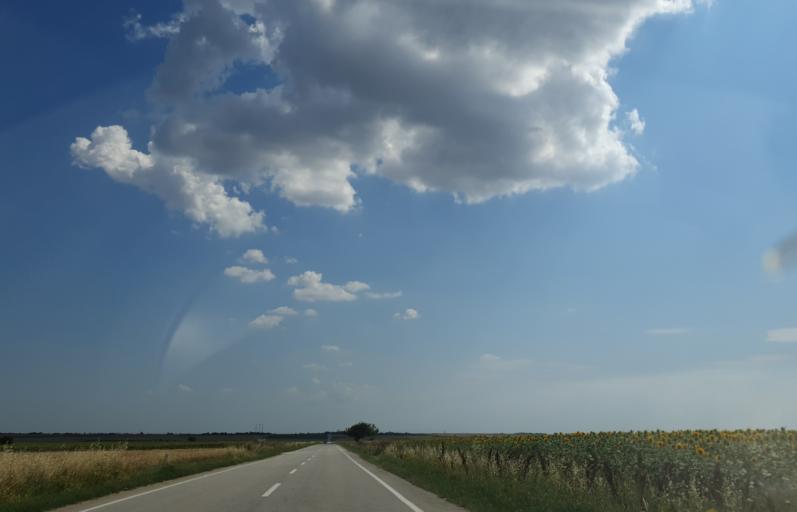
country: TR
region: Kirklareli
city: Buyukkaristiran
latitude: 41.4016
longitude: 27.5747
